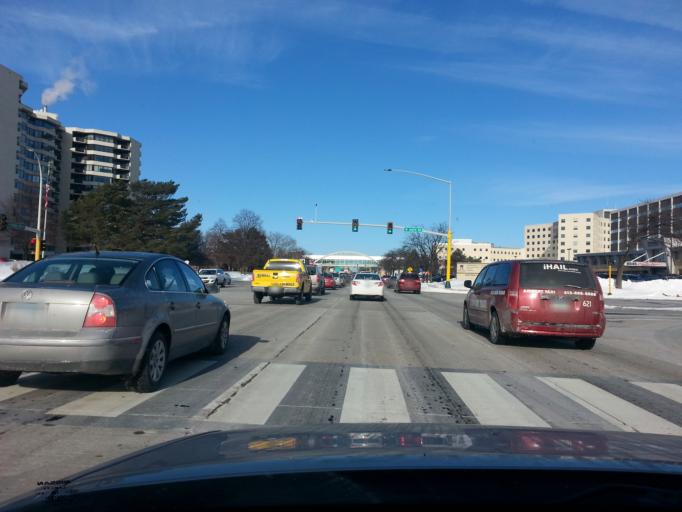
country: US
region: Minnesota
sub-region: Hennepin County
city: Edina
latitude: 44.8833
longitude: -93.3289
